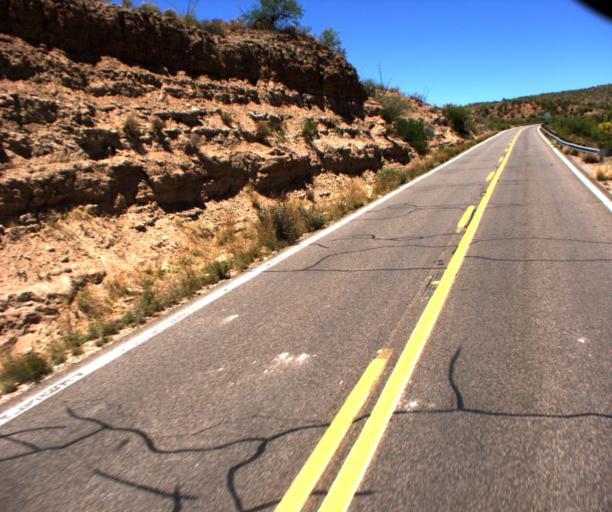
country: US
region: Arizona
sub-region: Pinal County
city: Kearny
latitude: 33.1514
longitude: -110.8040
